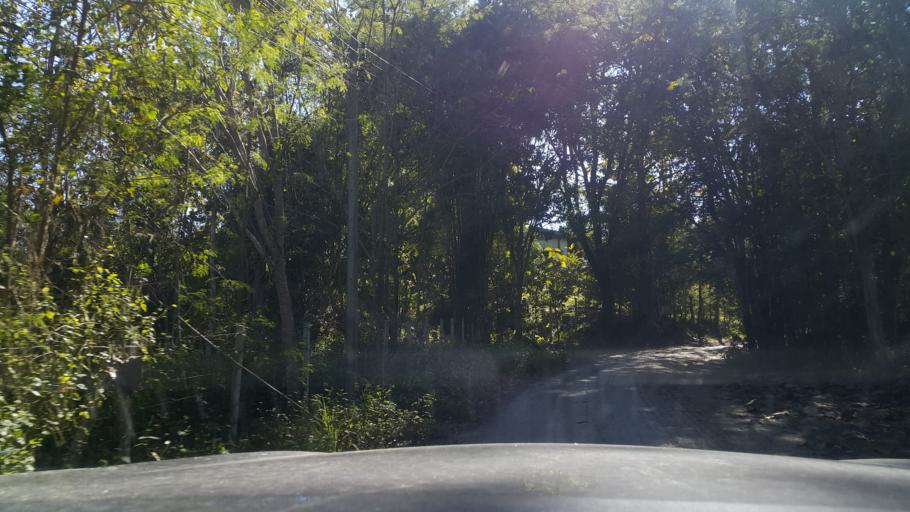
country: TH
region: Chiang Mai
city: Mae On
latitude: 18.7775
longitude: 99.2624
